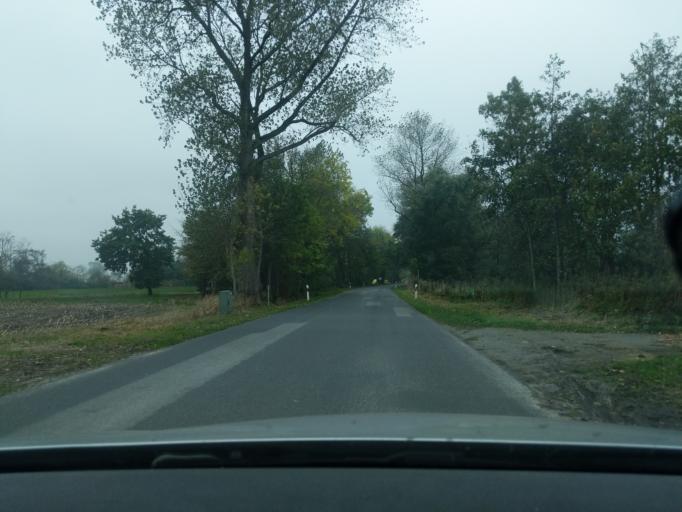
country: DE
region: Lower Saxony
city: Nordleda
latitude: 53.8274
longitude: 8.8141
